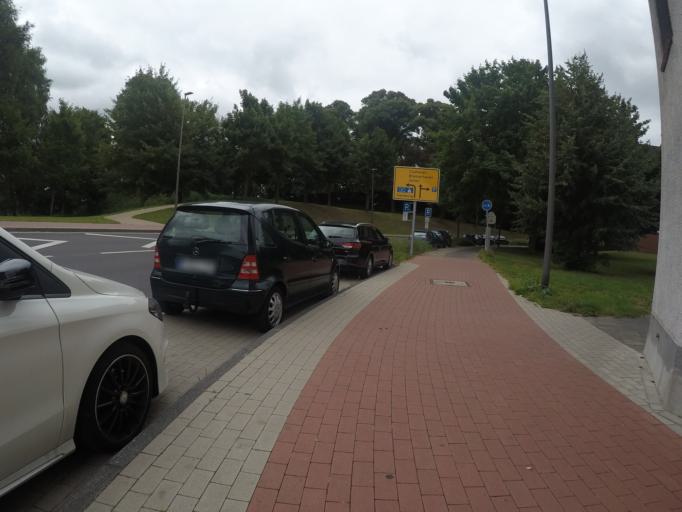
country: DE
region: Lower Saxony
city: Stade
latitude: 53.5993
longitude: 9.4803
